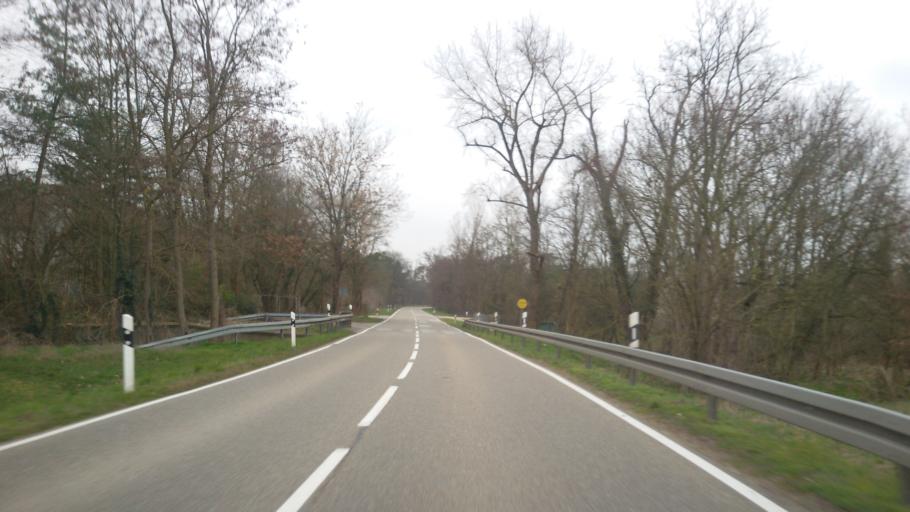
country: DE
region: Hesse
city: Lorsch
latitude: 49.6261
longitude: 8.5738
